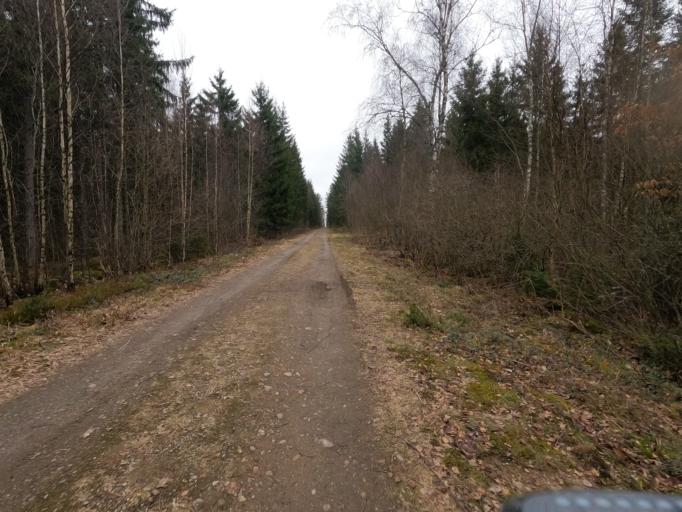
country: SE
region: Kronoberg
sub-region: Ljungby Kommun
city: Ljungby
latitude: 56.8252
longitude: 13.8813
